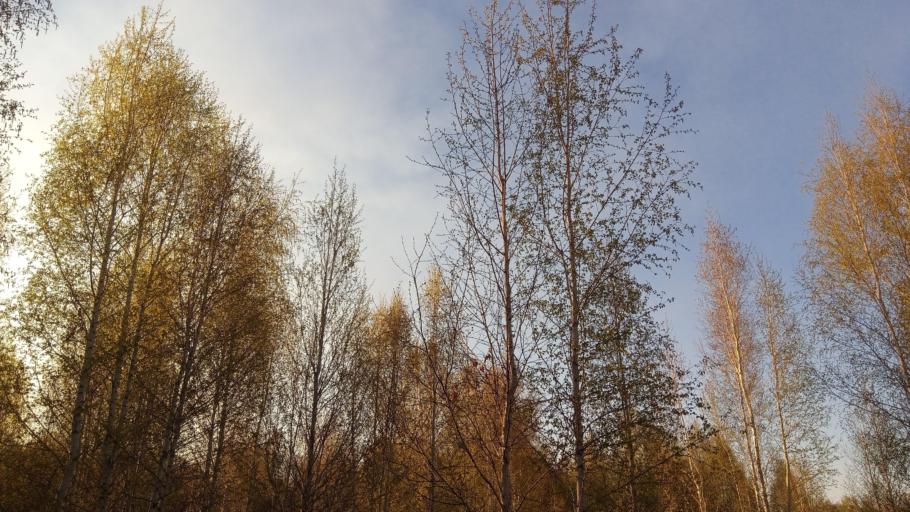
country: RU
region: Chelyabinsk
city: Timiryazevskiy
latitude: 54.9930
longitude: 60.8682
